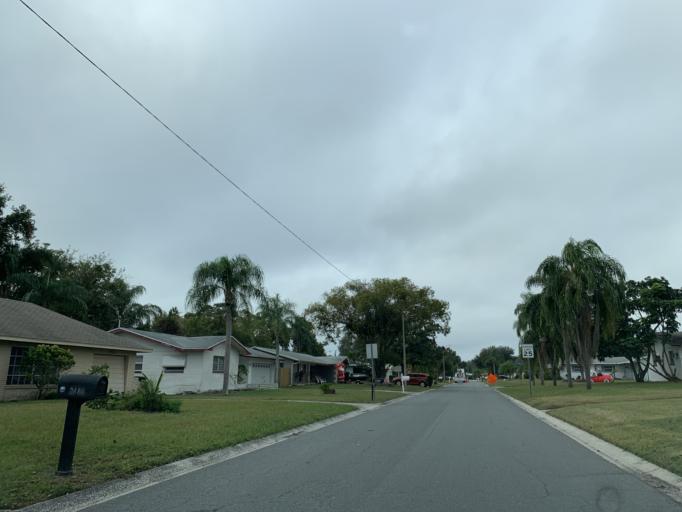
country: US
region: Florida
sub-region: Pinellas County
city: South Highpoint
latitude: 27.9499
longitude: -82.7348
